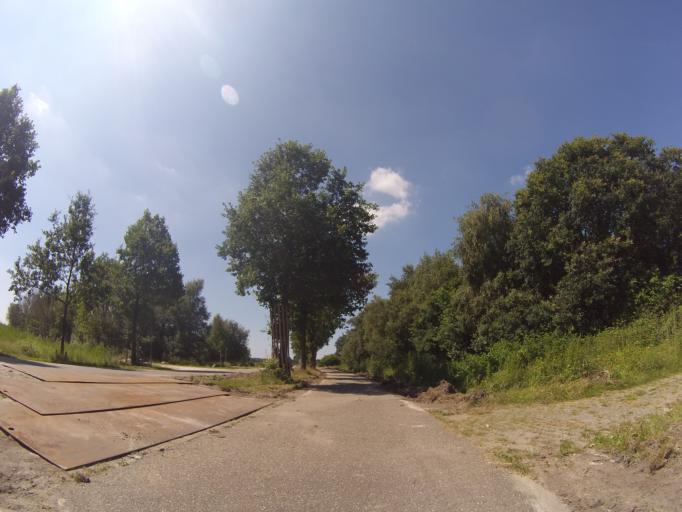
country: NL
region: Drenthe
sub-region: Gemeente Emmen
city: Klazienaveen
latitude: 52.7571
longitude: 6.9918
